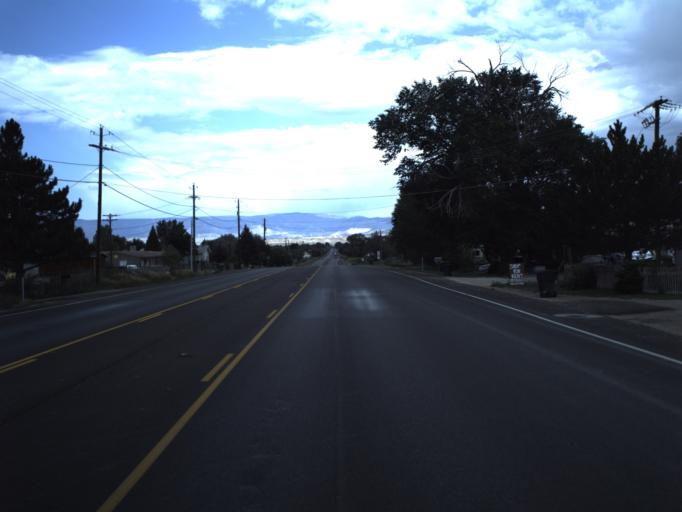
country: US
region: Utah
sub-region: Carbon County
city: Wellington
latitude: 39.5426
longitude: -110.6951
